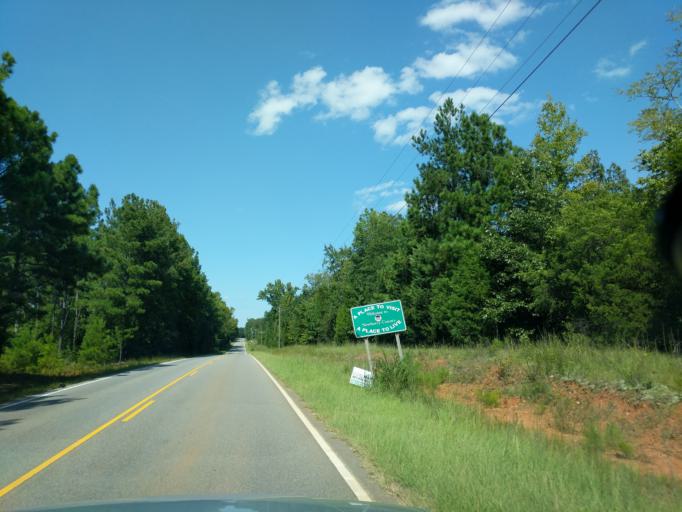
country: US
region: South Carolina
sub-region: Newberry County
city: Prosperity
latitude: 34.1070
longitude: -81.5651
